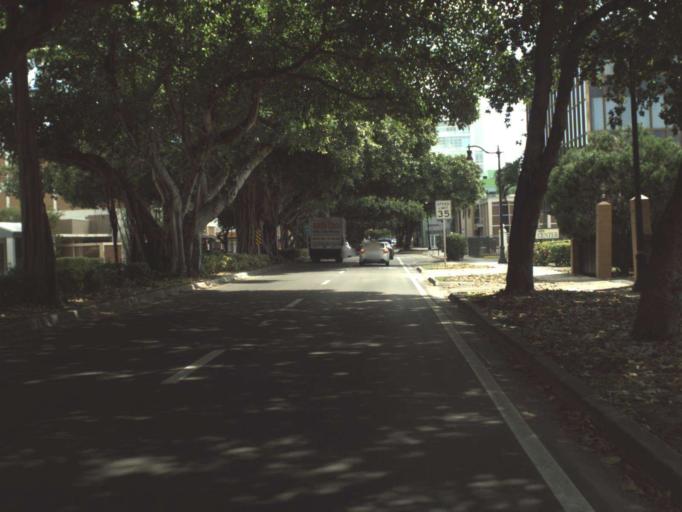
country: US
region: Florida
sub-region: Miami-Dade County
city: Miami
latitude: 25.7507
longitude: -80.2256
